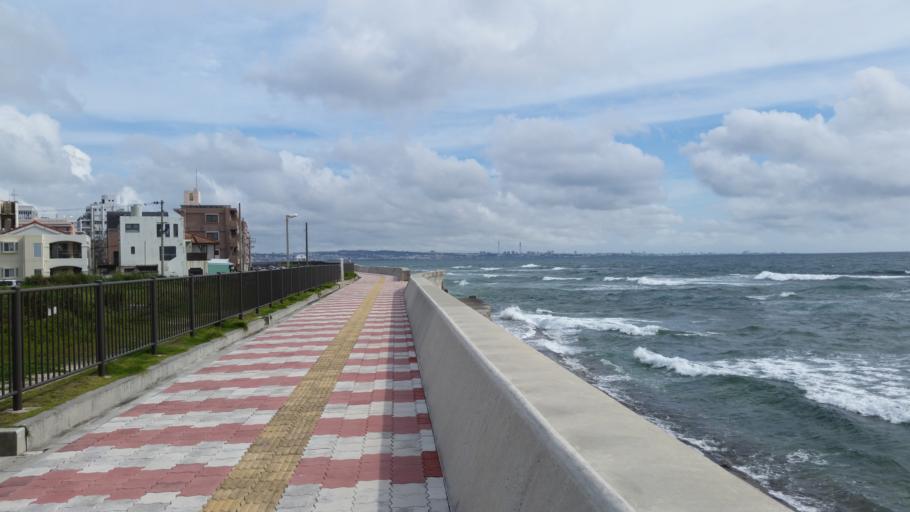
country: JP
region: Okinawa
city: Chatan
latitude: 26.3340
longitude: 127.7427
